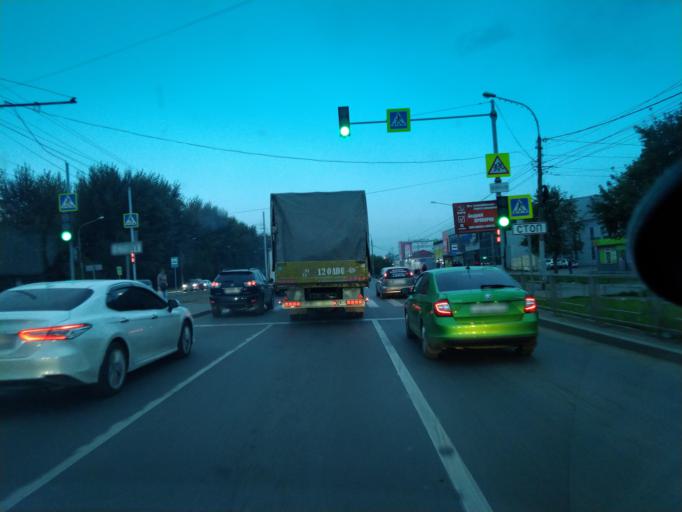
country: RU
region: Krasnoyarskiy
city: Berezovka
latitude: 56.0211
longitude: 93.0067
